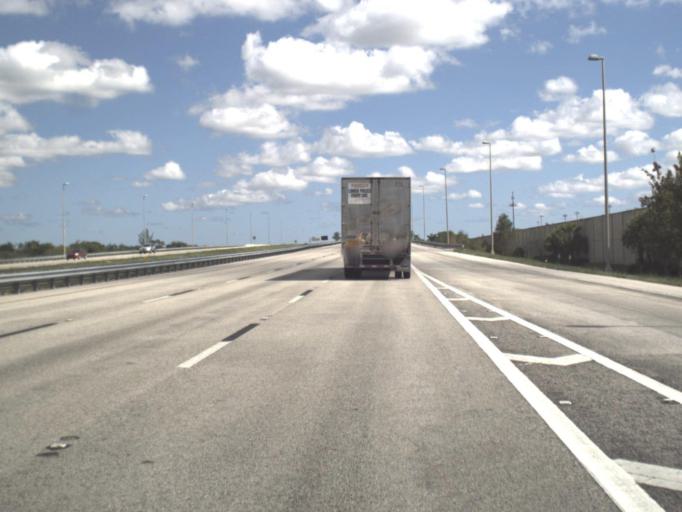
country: US
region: Florida
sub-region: Broward County
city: Coral Springs
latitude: 26.3020
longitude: -80.2719
